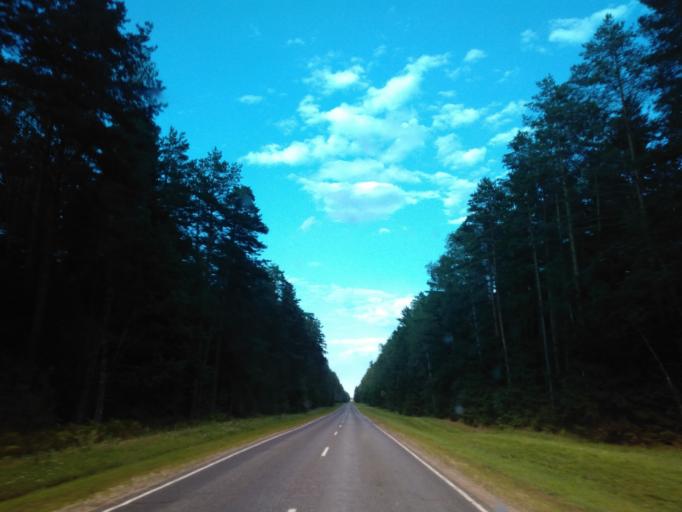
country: BY
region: Minsk
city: Uzda
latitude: 53.4261
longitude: 27.4457
